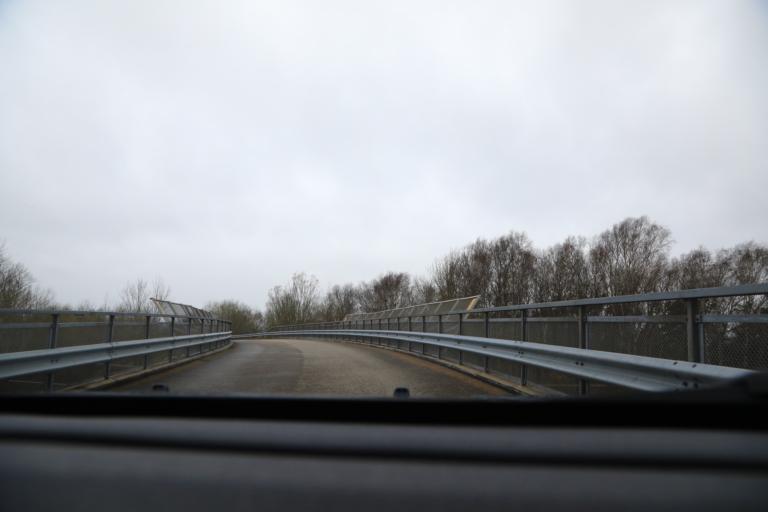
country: SE
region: Halland
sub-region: Kungsbacka Kommun
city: Frillesas
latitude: 57.2988
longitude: 12.1678
